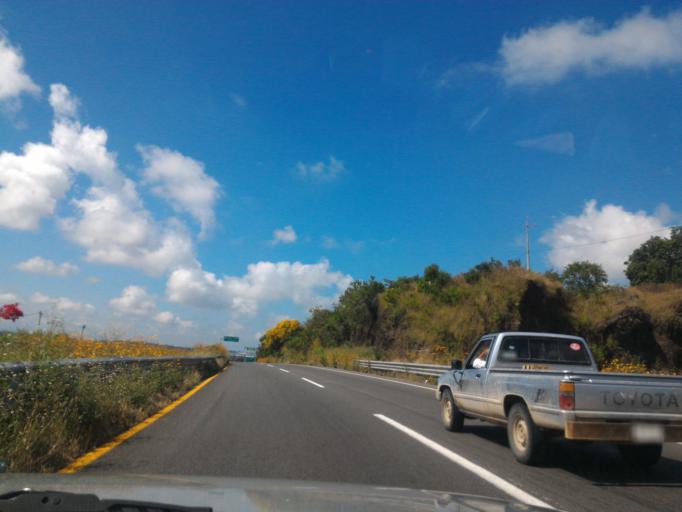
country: MX
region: Jalisco
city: La Venta del Astillero
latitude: 20.7365
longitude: -103.5957
